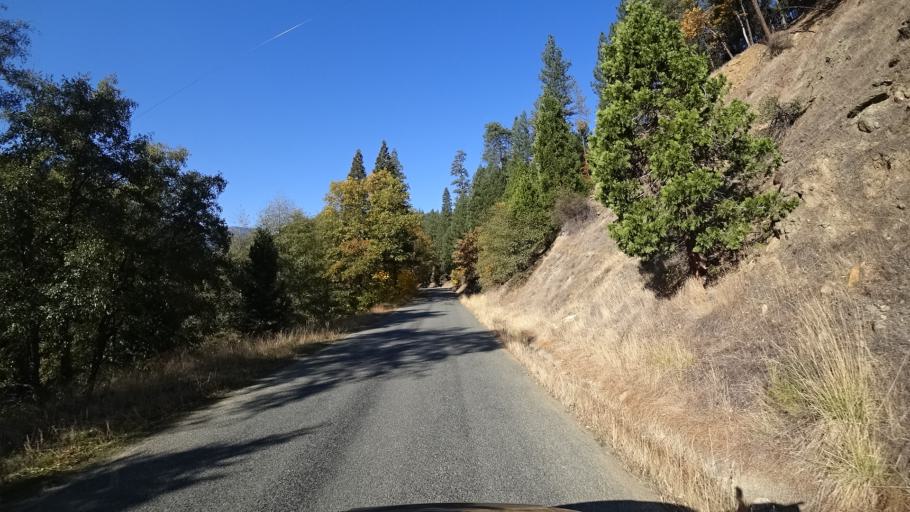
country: US
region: California
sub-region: Siskiyou County
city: Happy Camp
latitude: 41.6360
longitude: -123.0771
